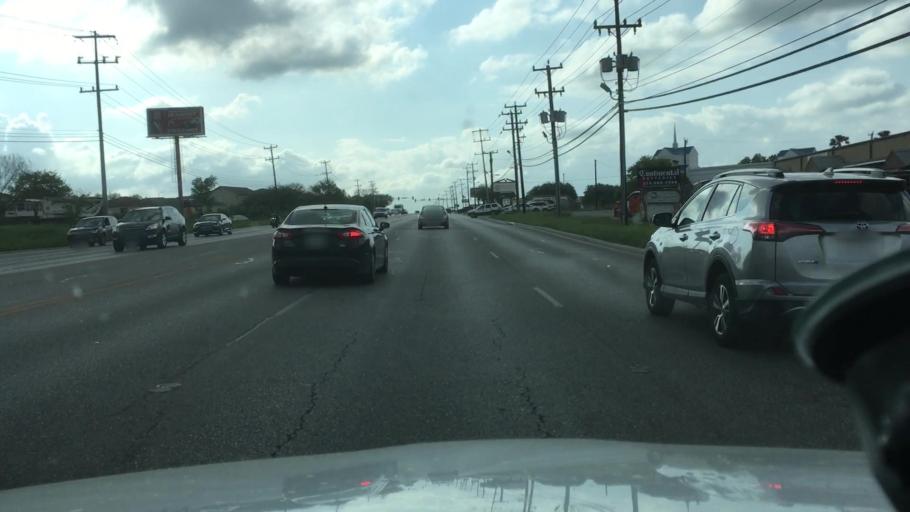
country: US
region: Texas
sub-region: Bexar County
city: Windcrest
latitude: 29.5009
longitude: -98.3559
